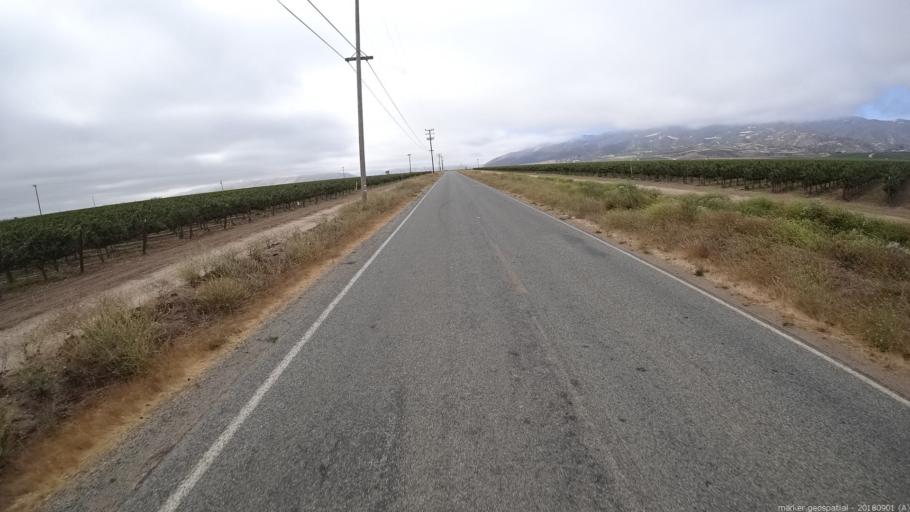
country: US
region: California
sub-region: Monterey County
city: Soledad
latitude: 36.3520
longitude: -121.3205
